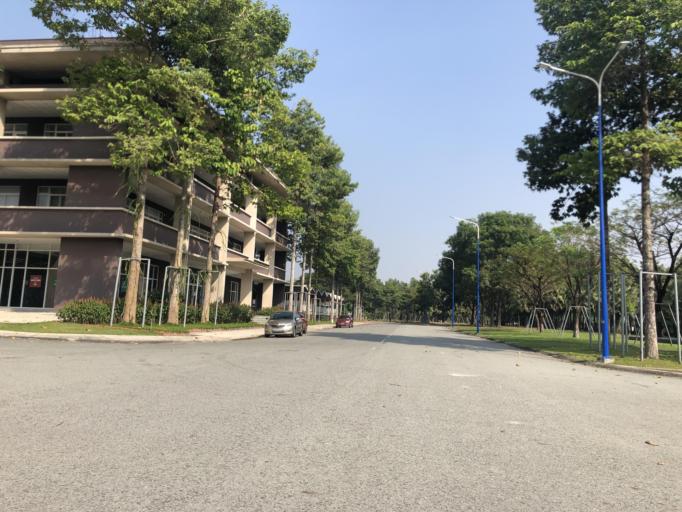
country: VN
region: Binh Duong
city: Thu Dau Mot
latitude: 11.0532
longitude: 106.6681
